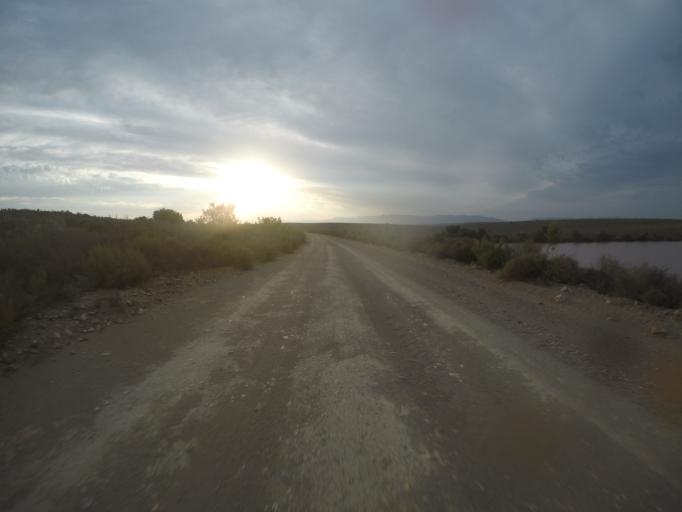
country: ZA
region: Eastern Cape
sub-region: Cacadu District Municipality
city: Willowmore
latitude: -33.5780
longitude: 23.1756
